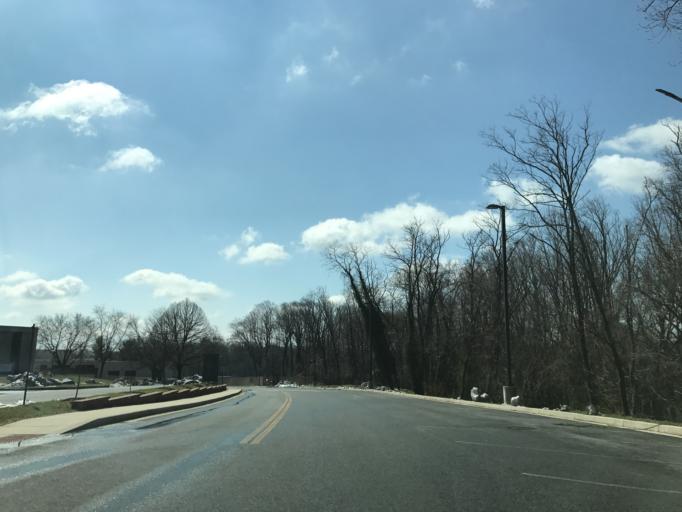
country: US
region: Maryland
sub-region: Baltimore County
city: Catonsville
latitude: 39.2529
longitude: -76.7371
